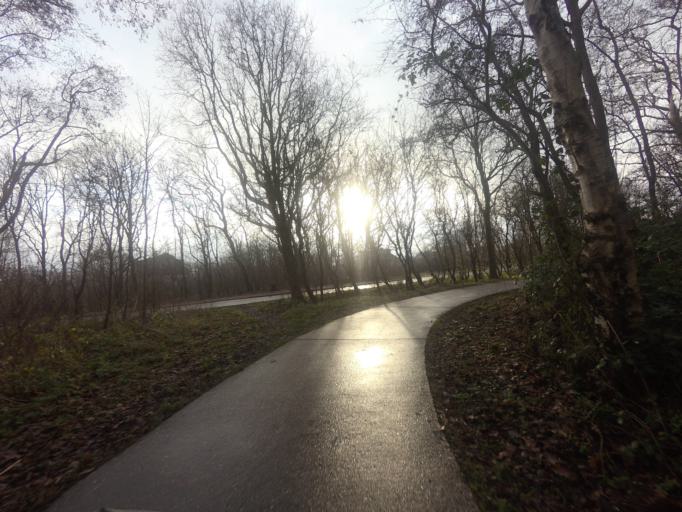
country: NL
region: North Holland
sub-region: Gemeente Texel
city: Den Burg
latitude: 53.1559
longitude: 4.8467
